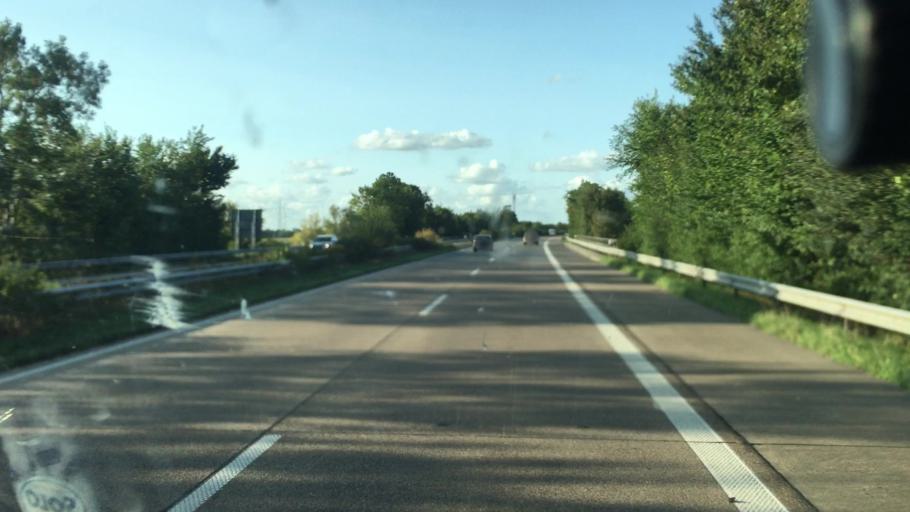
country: DE
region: Lower Saxony
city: Sande
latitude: 53.4588
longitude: 8.0189
